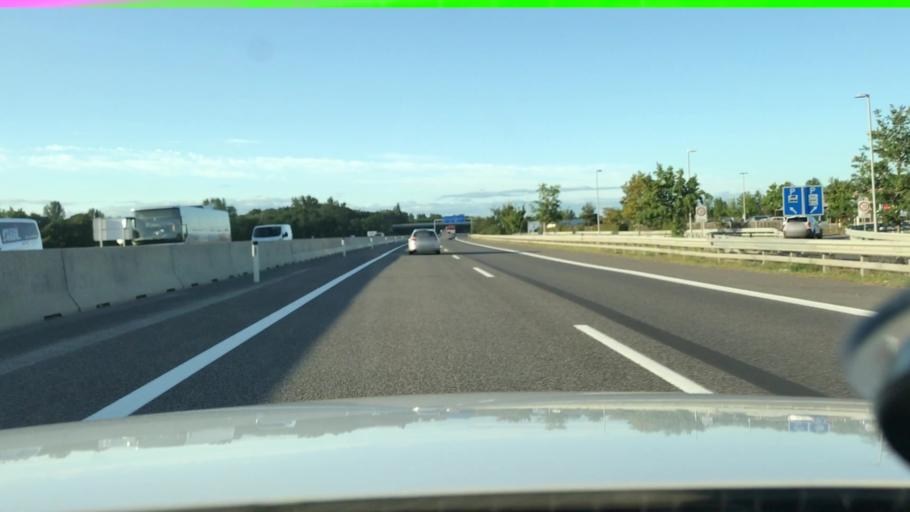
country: AT
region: Lower Austria
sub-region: Politischer Bezirk Sankt Polten
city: Herzogenburg
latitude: 48.3120
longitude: 15.7158
